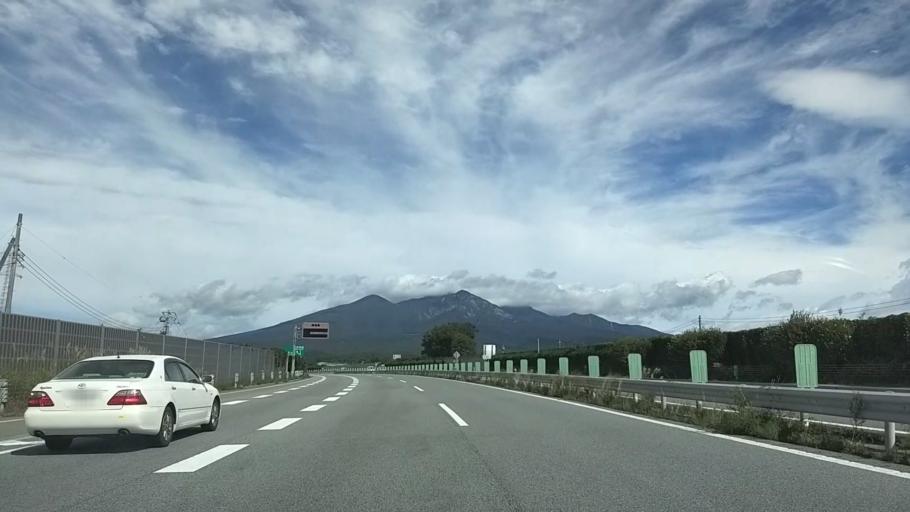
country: JP
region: Yamanashi
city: Nirasaki
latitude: 35.8316
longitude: 138.3924
